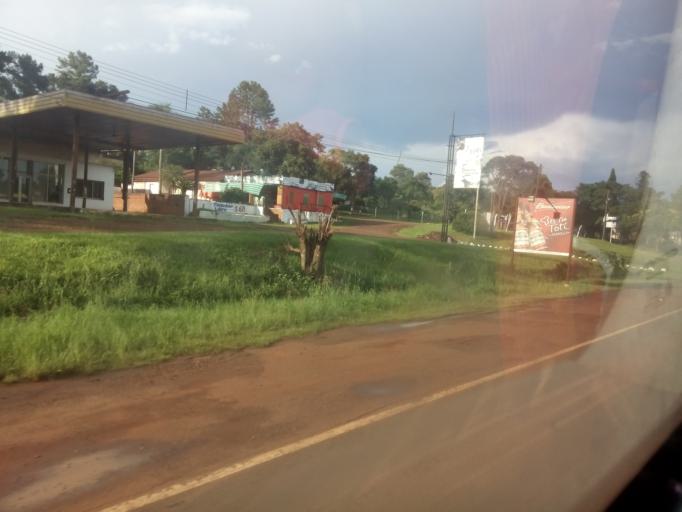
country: AR
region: Misiones
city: Santa Ana
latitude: -27.3794
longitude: -55.5798
